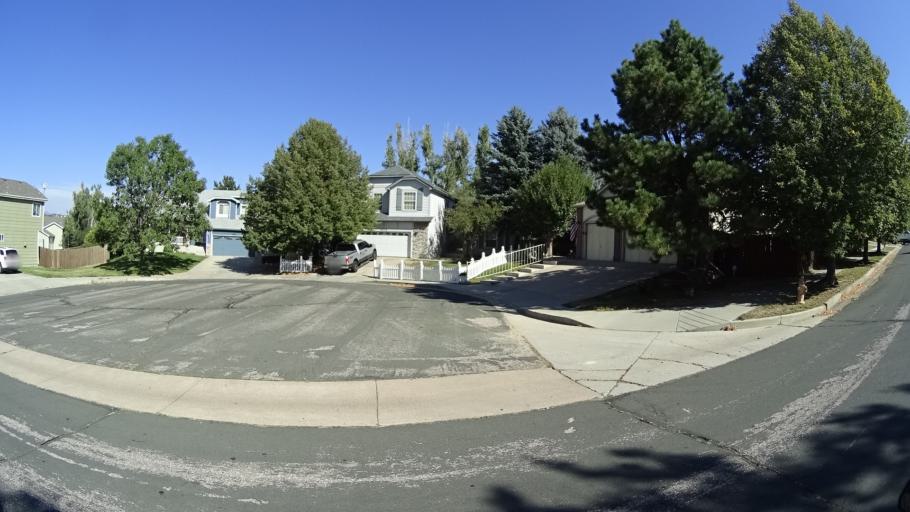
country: US
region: Colorado
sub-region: El Paso County
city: Cimarron Hills
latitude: 38.8770
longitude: -104.7046
